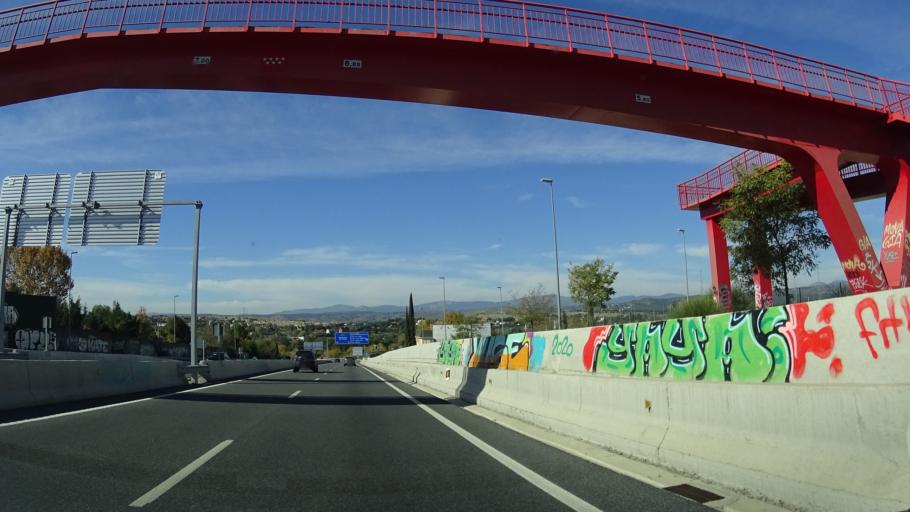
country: ES
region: Madrid
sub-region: Provincia de Madrid
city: Villanueva del Pardillo
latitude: 40.4841
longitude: -3.9318
